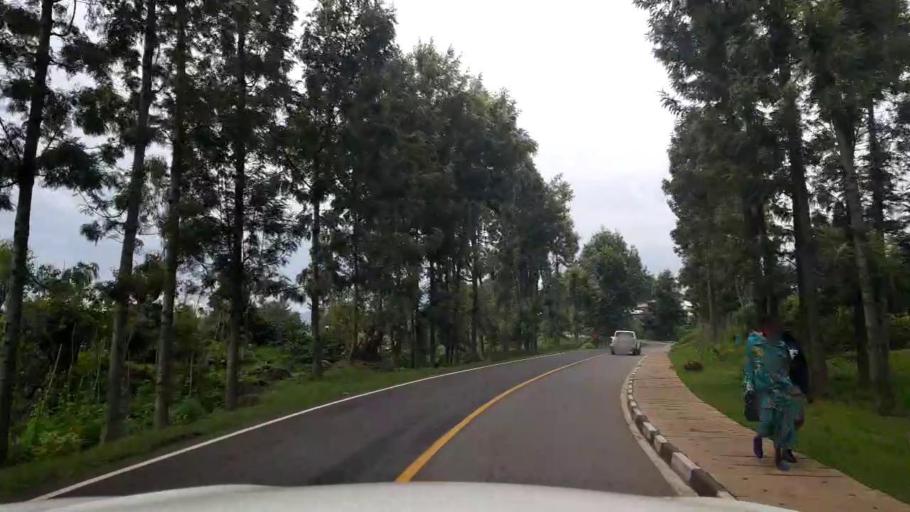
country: RW
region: Northern Province
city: Musanze
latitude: -1.4522
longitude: 29.6046
